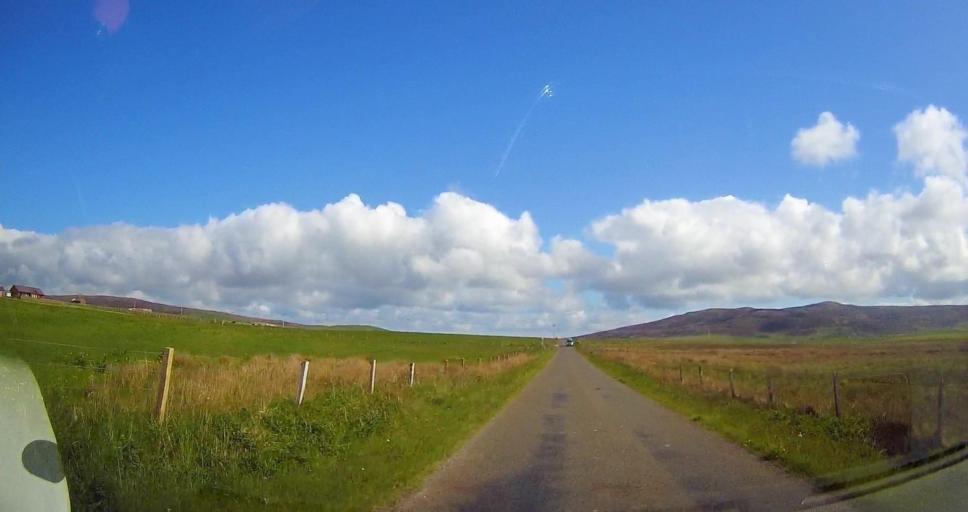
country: GB
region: Scotland
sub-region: Orkney Islands
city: Stromness
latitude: 58.9928
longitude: -3.1573
